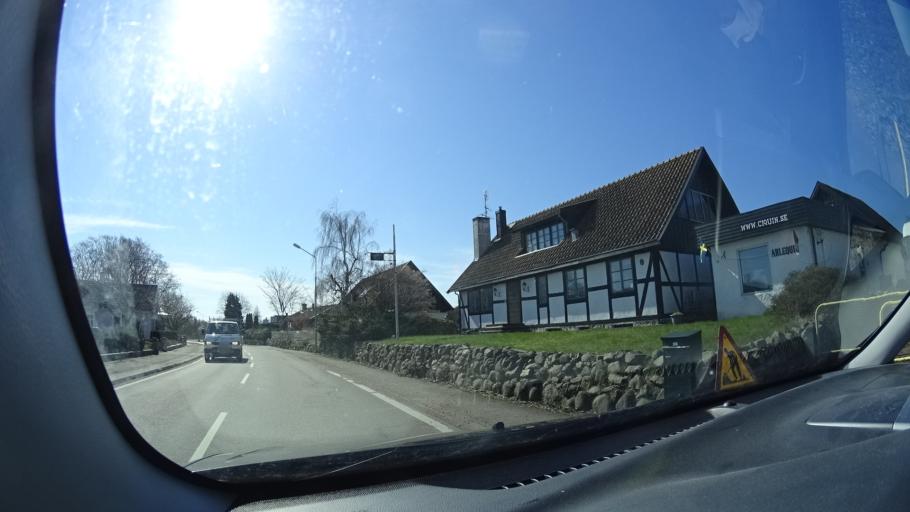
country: SE
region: Skane
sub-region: Hoganas Kommun
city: Hoganas
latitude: 56.2210
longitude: 12.6760
